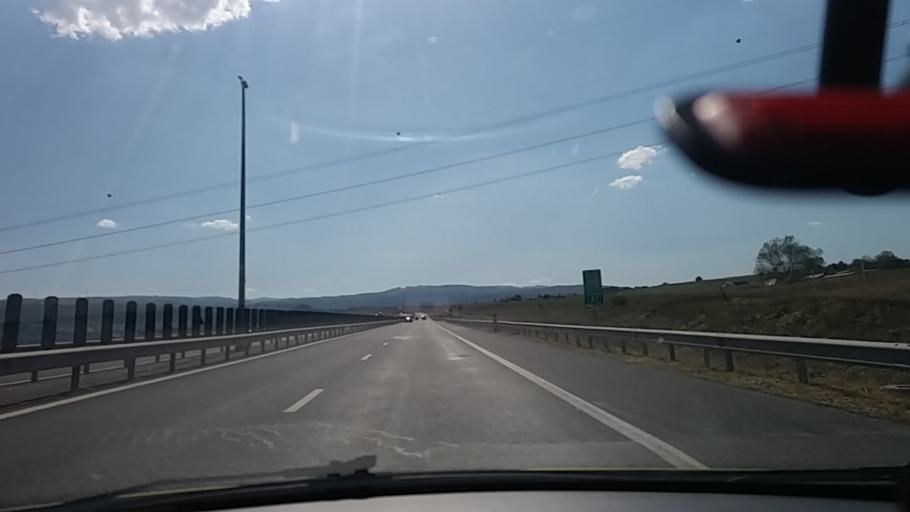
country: RO
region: Sibiu
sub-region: Comuna Apoldu de Jos
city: Apoldu de Jos
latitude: 45.8472
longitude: 23.8692
